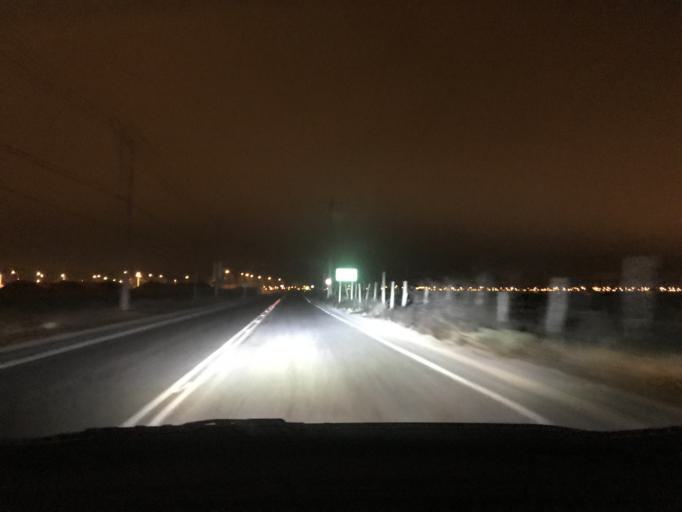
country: CL
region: Coquimbo
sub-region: Provincia de Elqui
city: La Serena
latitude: -29.9233
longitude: -71.2260
